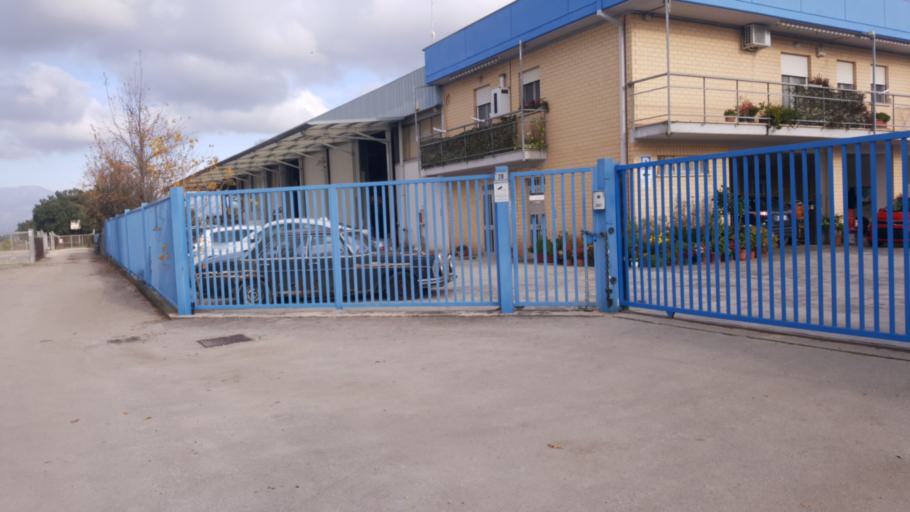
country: IT
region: Latium
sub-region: Provincia di Latina
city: Latina
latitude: 41.4757
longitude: 12.8857
